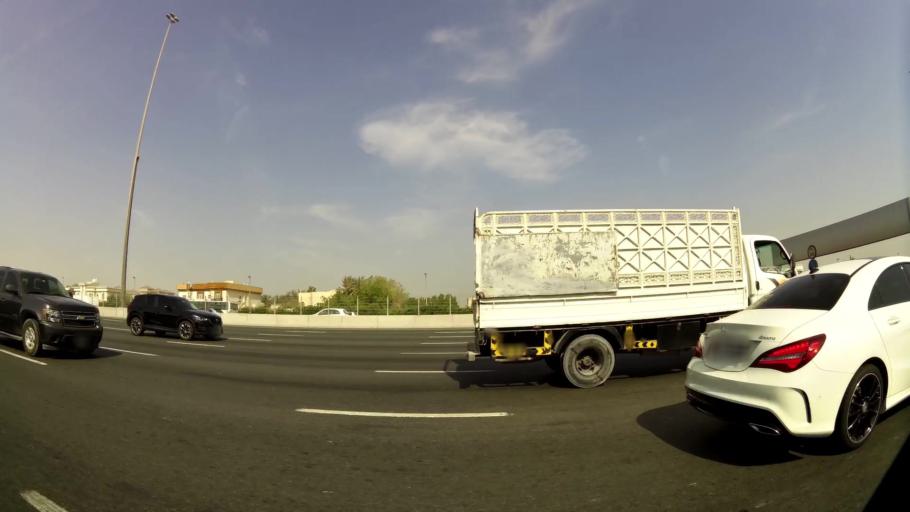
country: AE
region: Ash Shariqah
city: Sharjah
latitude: 25.2430
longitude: 55.4049
